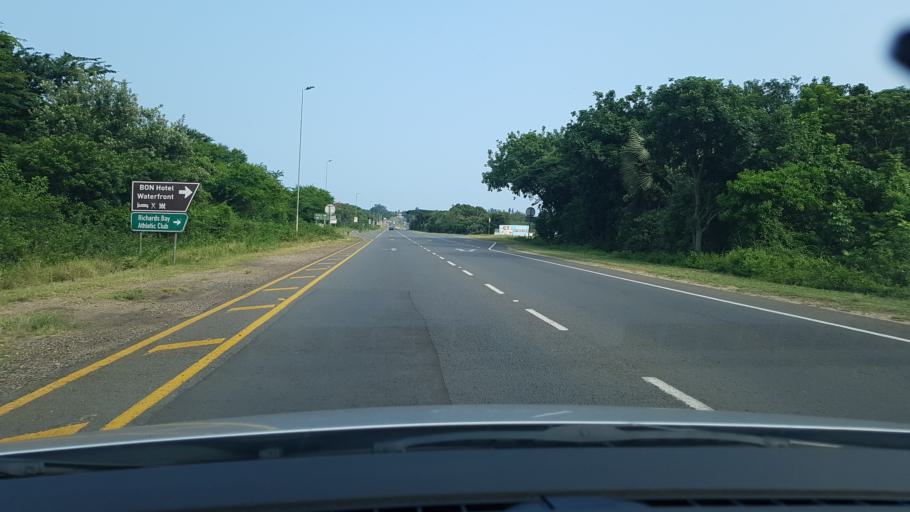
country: ZA
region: KwaZulu-Natal
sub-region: uThungulu District Municipality
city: Richards Bay
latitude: -28.7824
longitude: 32.0845
